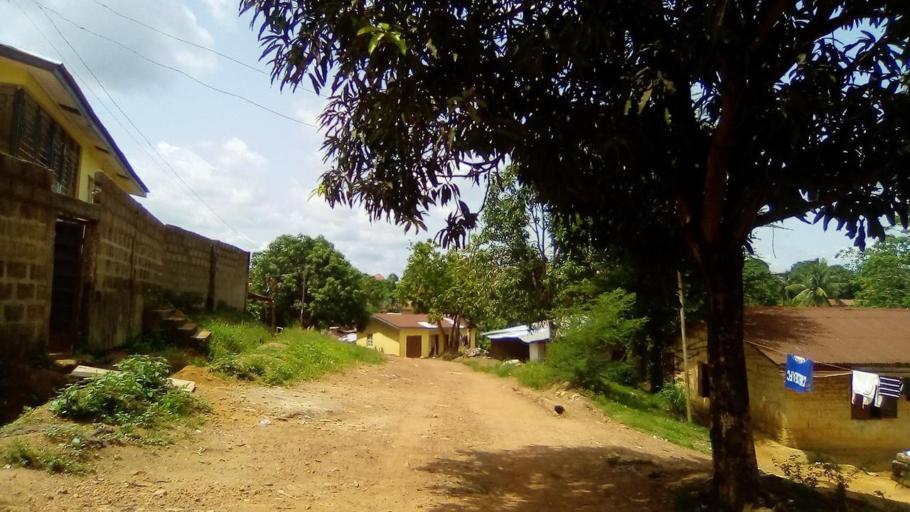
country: SL
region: Southern Province
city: Bo
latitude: 7.9662
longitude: -11.7292
